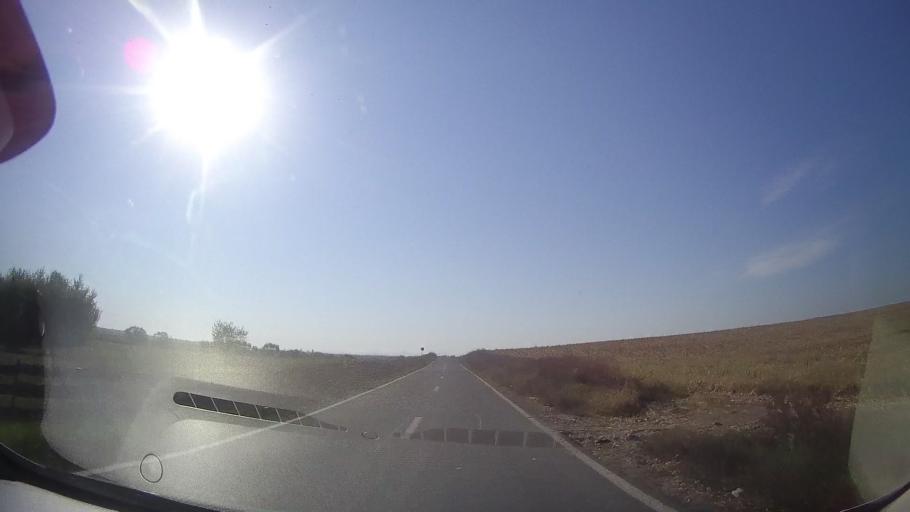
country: RO
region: Timis
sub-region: Comuna Topolovatu Mare
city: Topolovatu Mare
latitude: 45.8010
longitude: 21.5859
